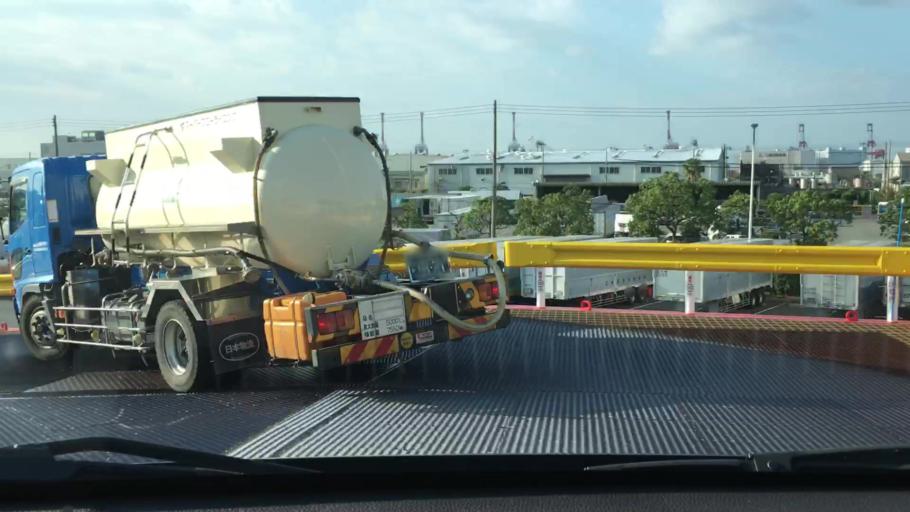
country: JP
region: Hyogo
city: Ashiya
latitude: 34.6968
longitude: 135.2834
